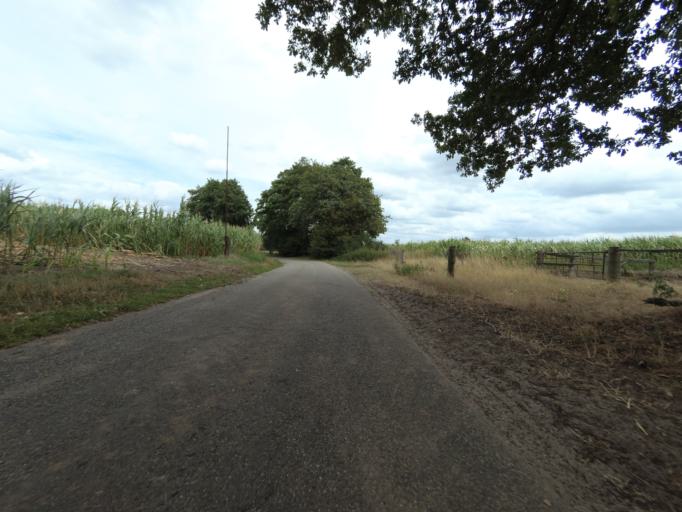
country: DE
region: North Rhine-Westphalia
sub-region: Regierungsbezirk Munster
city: Ahaus
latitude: 52.1097
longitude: 7.0104
